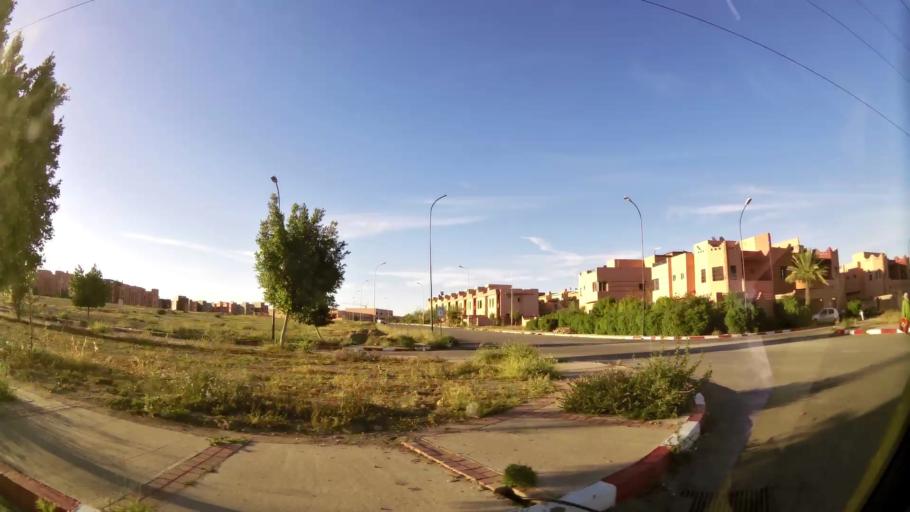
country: MA
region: Marrakech-Tensift-Al Haouz
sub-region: Marrakech
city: Marrakesh
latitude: 31.7427
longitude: -8.1139
